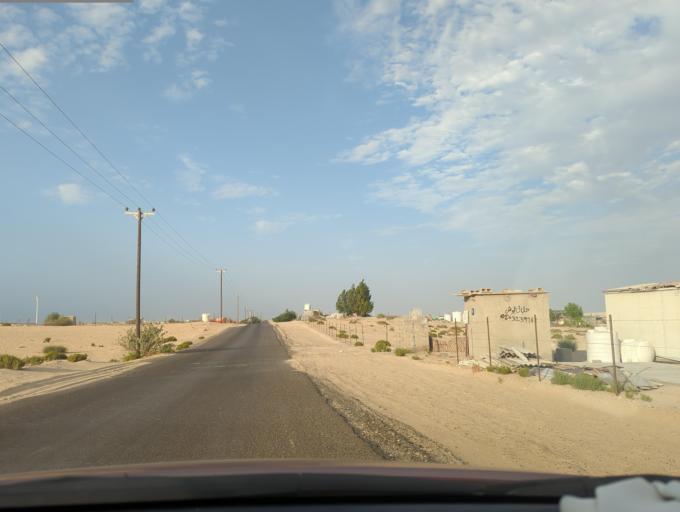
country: AE
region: Dubai
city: Dubai
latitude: 24.7142
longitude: 54.8685
